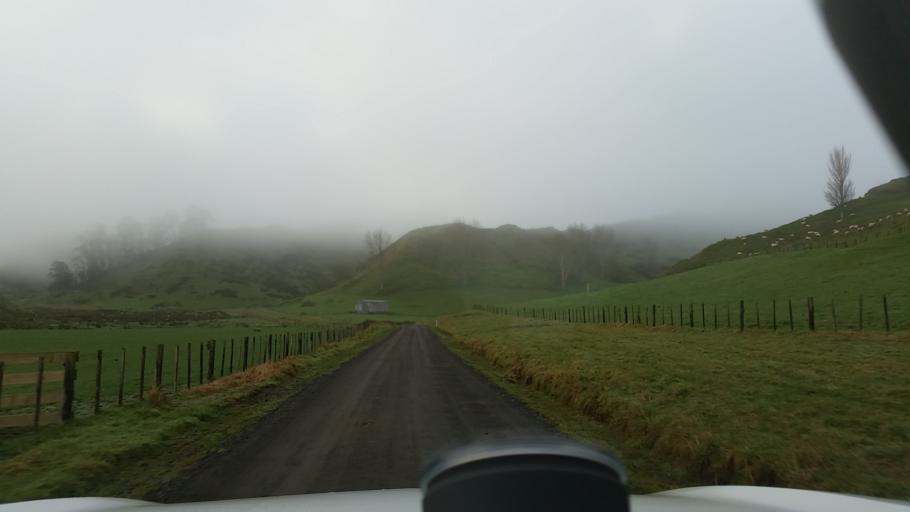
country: NZ
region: Taranaki
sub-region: South Taranaki District
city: Eltham
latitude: -39.4292
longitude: 174.4398
